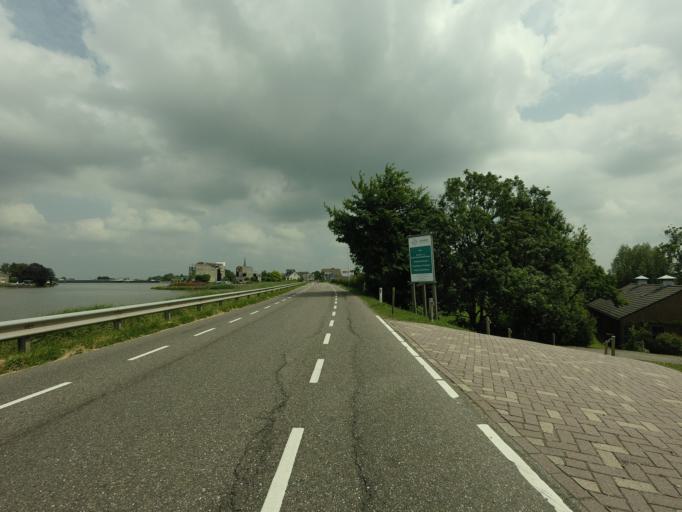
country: NL
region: South Holland
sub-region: Gemeente Krimpen aan den IJssel
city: Krimpen aan den IJssel
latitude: 51.9354
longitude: 4.6276
